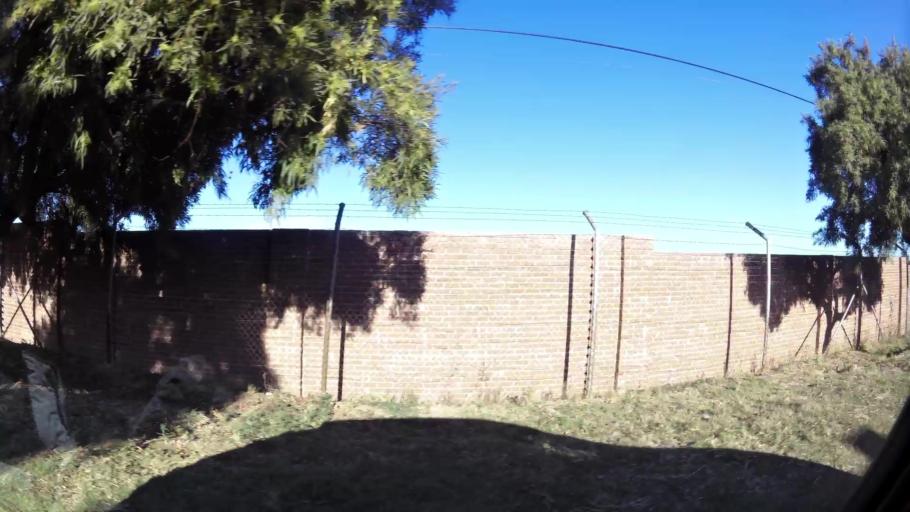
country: ZA
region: Gauteng
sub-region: City of Johannesburg Metropolitan Municipality
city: Midrand
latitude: -26.0353
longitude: 28.1576
